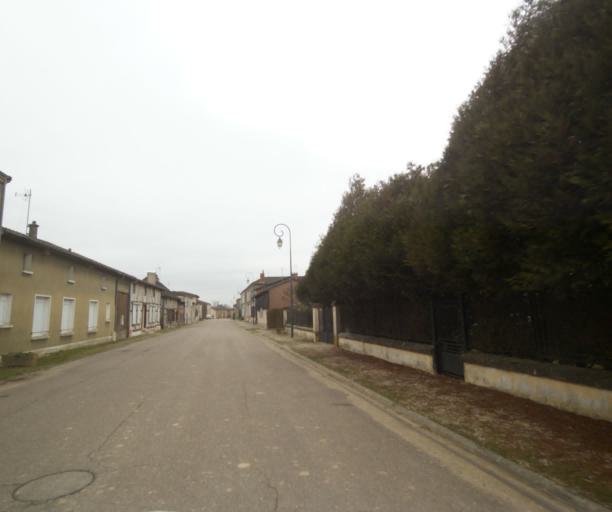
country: FR
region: Champagne-Ardenne
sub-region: Departement de la Haute-Marne
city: Villiers-en-Lieu
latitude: 48.6378
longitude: 4.7713
